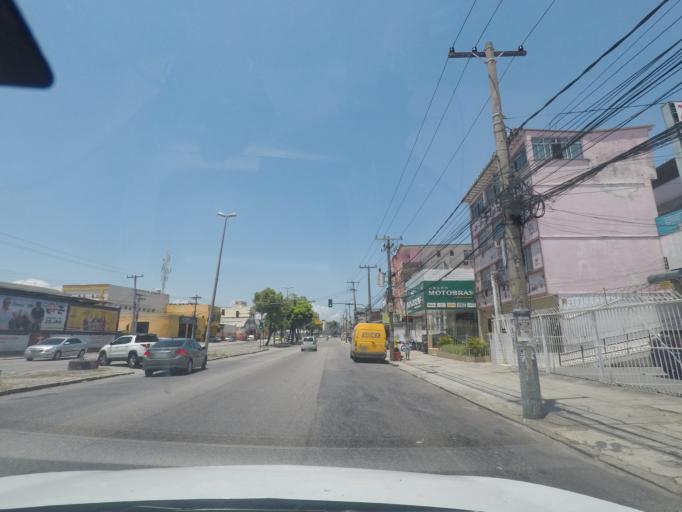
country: BR
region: Rio de Janeiro
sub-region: Rio De Janeiro
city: Rio de Janeiro
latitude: -22.8831
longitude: -43.2961
